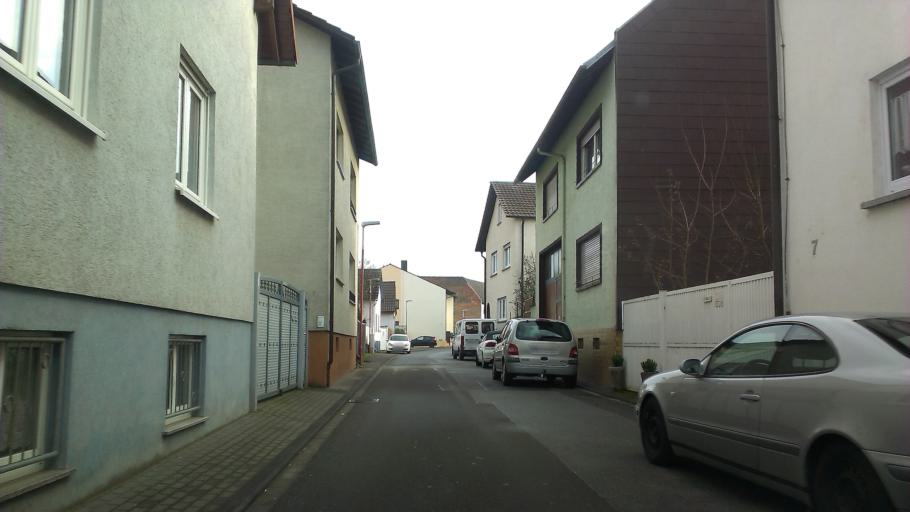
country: DE
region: Baden-Wuerttemberg
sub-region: Karlsruhe Region
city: Ubstadt-Weiher
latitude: 49.1454
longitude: 8.6702
